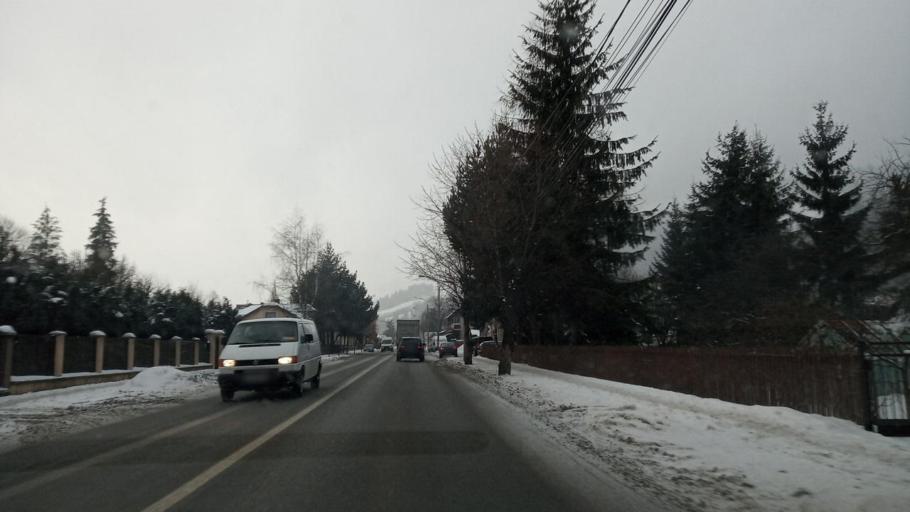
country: RO
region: Suceava
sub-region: Municipiul Vatra Dornei
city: Vatra Dornei
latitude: 47.3473
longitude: 25.3420
